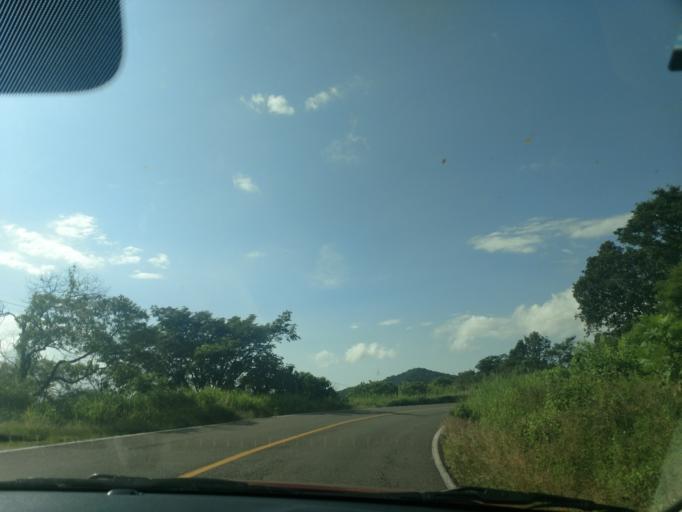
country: MX
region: Jalisco
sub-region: Atengo
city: Soyatlan del Oro
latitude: 20.4900
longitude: -104.3616
